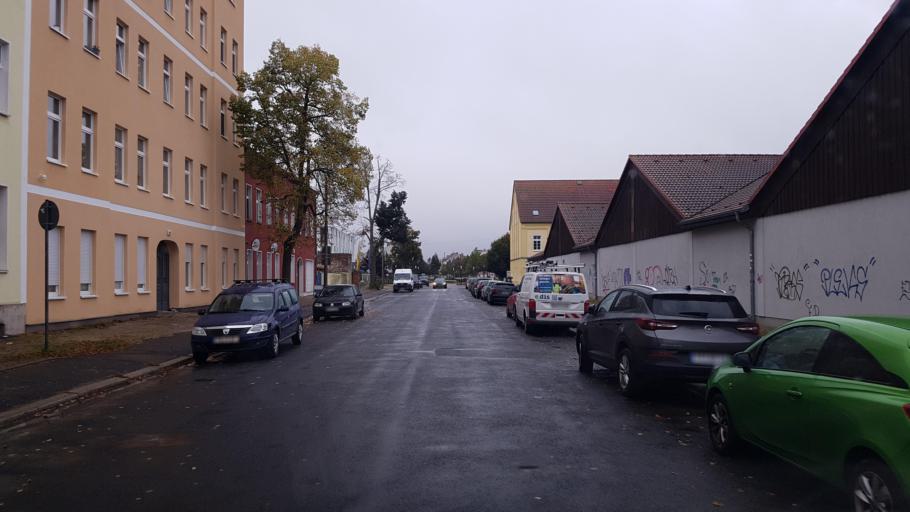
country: DE
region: Brandenburg
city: Furstenwalde
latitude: 52.3685
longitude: 14.0611
